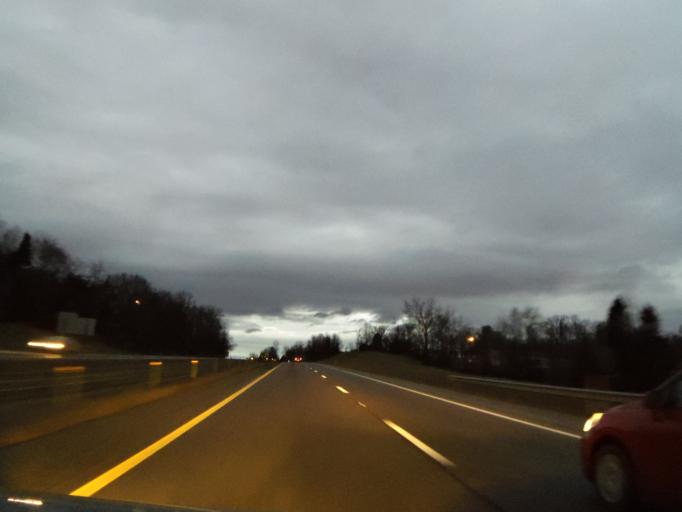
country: US
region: Tennessee
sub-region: Washington County
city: Gray
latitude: 36.4153
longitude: -82.4896
